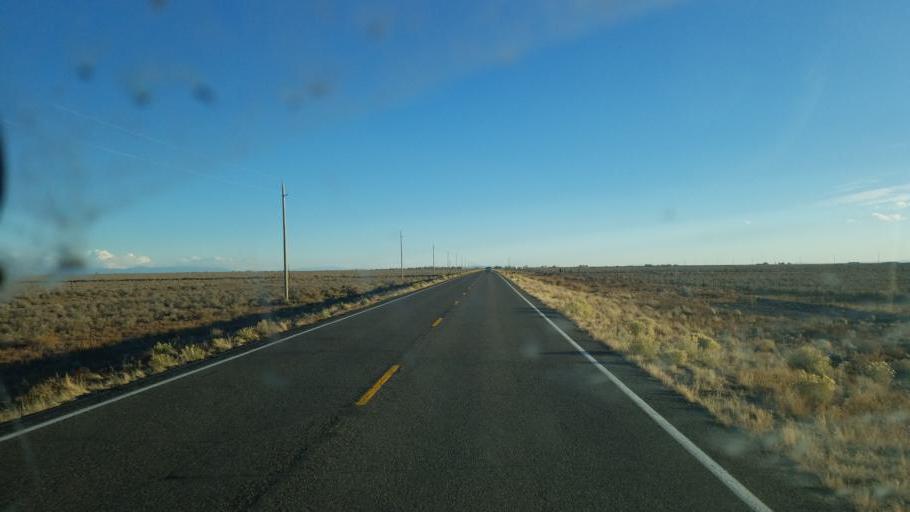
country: US
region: Colorado
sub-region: Saguache County
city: Center
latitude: 37.7806
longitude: -105.8844
